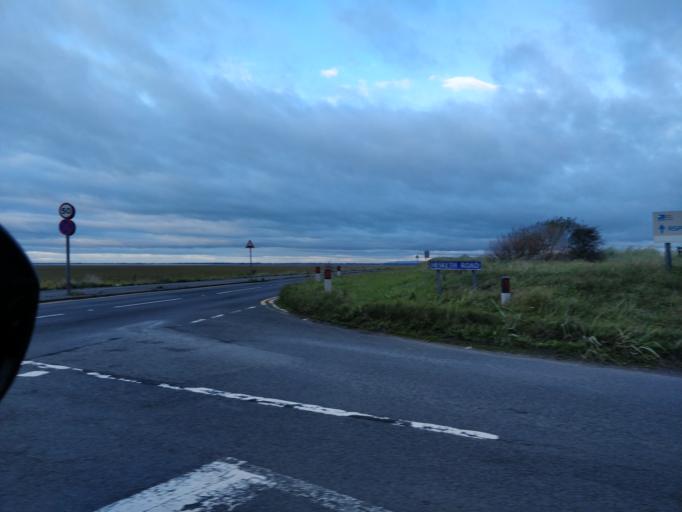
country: GB
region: England
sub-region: Sefton
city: Southport
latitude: 53.6669
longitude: -2.9926
